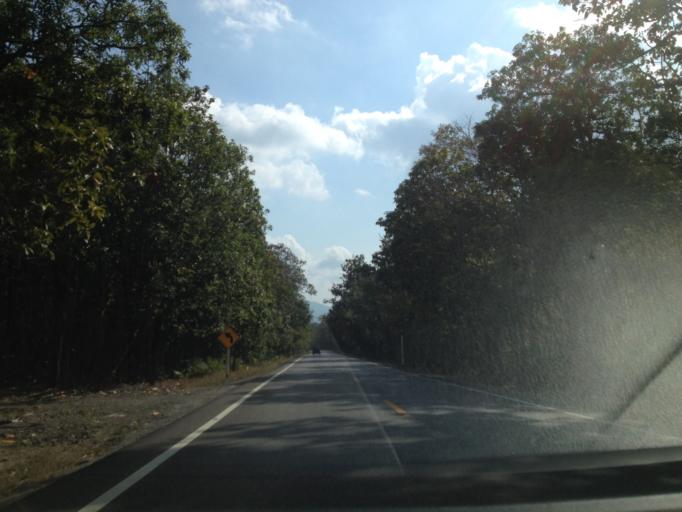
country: TH
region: Chiang Mai
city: Hot
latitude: 18.1514
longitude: 98.4191
